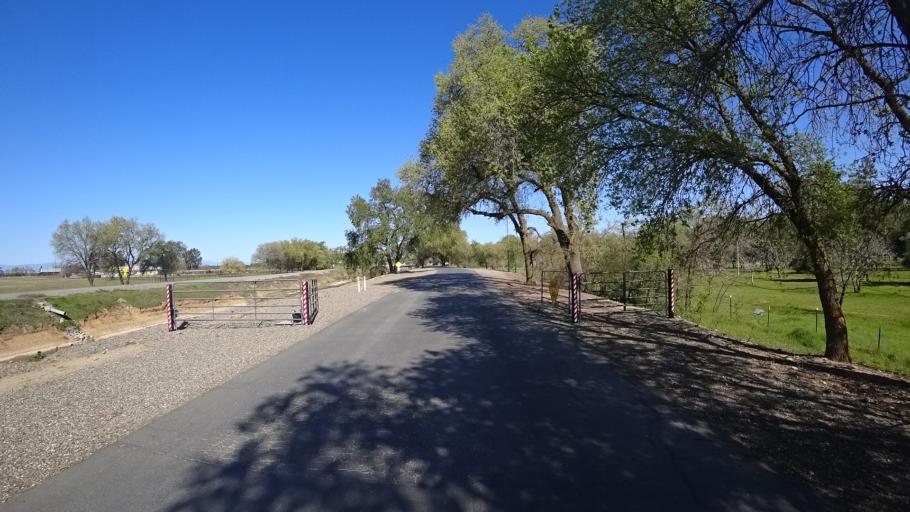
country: US
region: California
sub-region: Glenn County
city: Hamilton City
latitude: 39.7849
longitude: -122.0464
